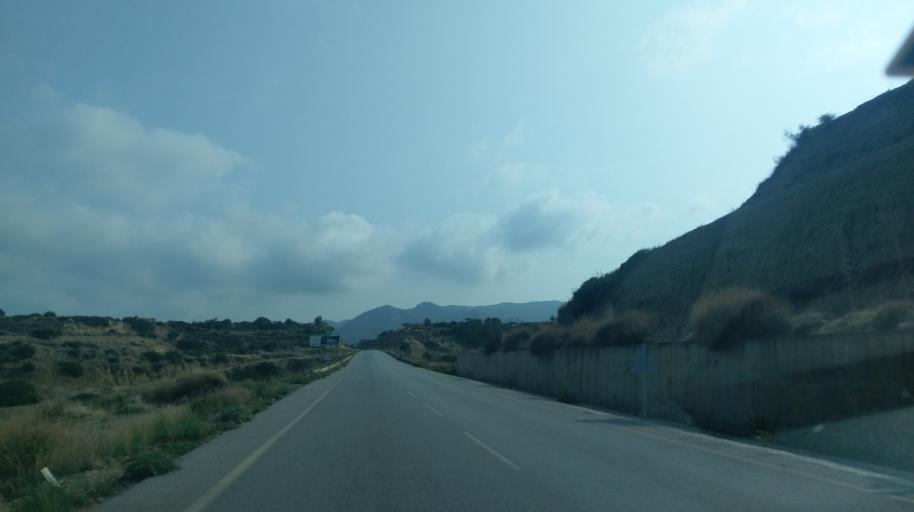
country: CY
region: Ammochostos
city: Lefkonoiko
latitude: 35.3536
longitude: 33.6204
